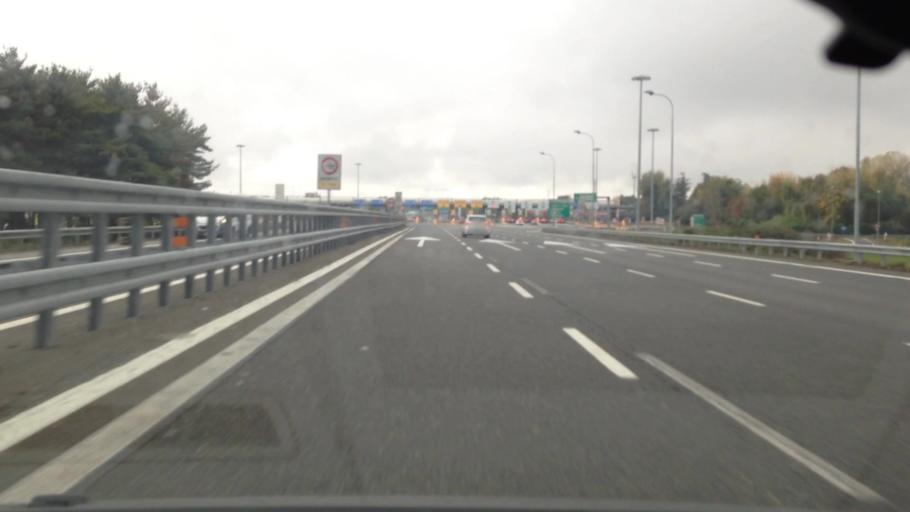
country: IT
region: Piedmont
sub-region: Provincia di Asti
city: Villanova d'Asti
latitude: 44.9526
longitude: 7.9275
